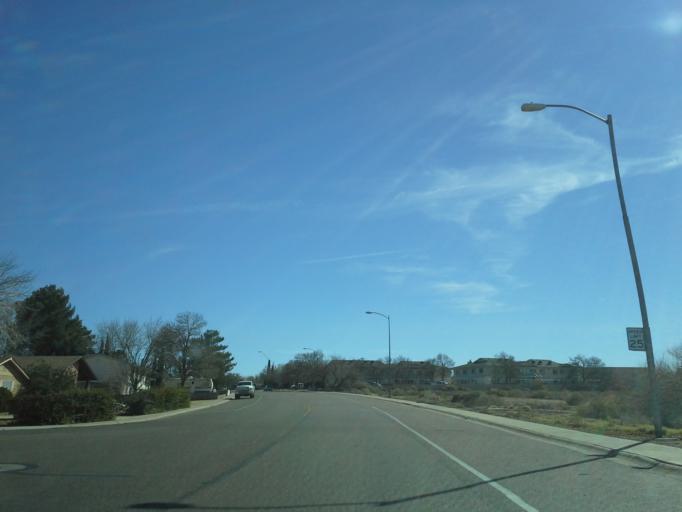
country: US
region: Arizona
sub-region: Coconino County
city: Page
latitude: 36.9270
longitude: -111.4600
